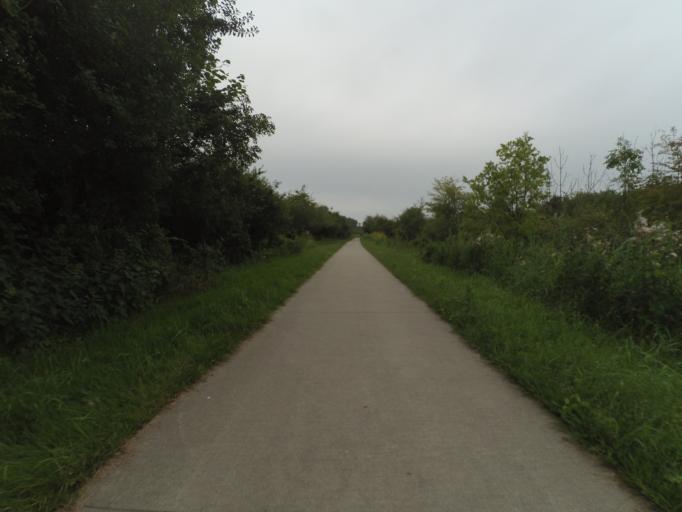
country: NL
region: Flevoland
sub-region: Gemeente Almere
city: Almere Stad
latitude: 52.4232
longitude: 5.2769
